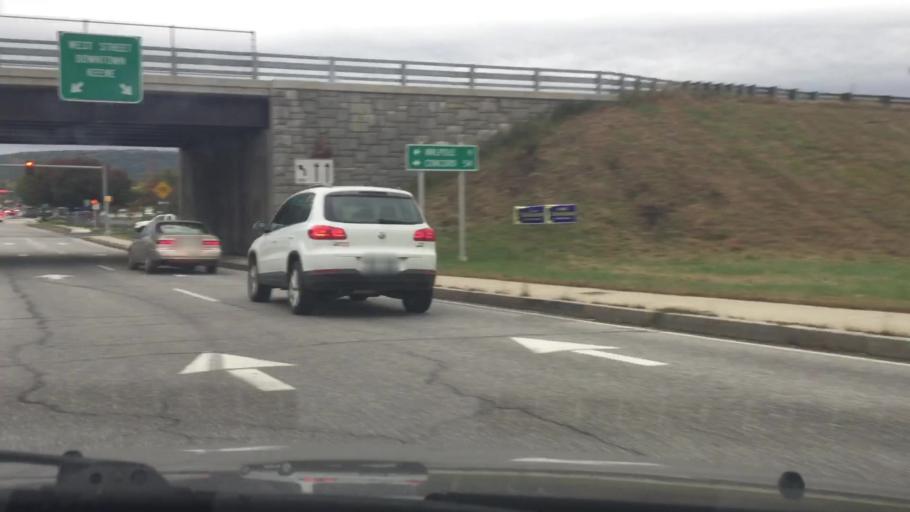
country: US
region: New Hampshire
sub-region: Cheshire County
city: Keene
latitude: 42.9336
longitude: -72.2979
